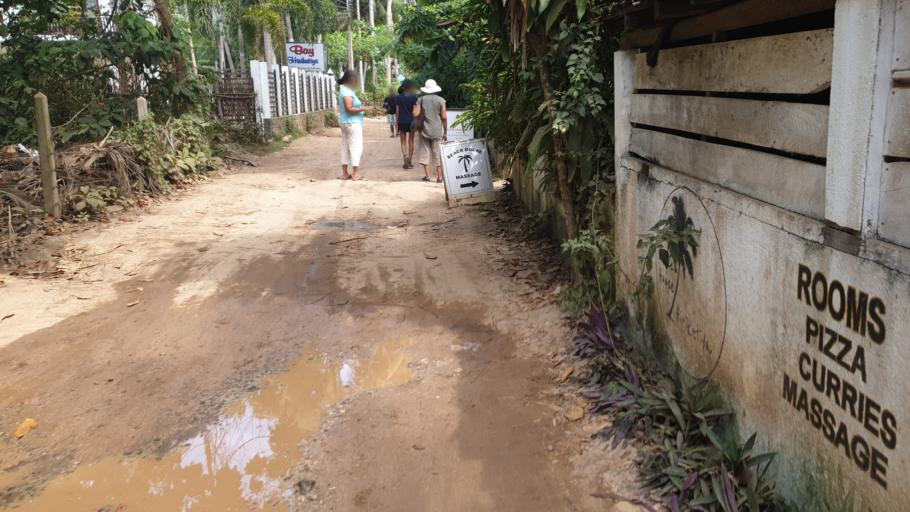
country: LK
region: Southern
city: Tangalla
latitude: 5.9628
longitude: 80.7069
